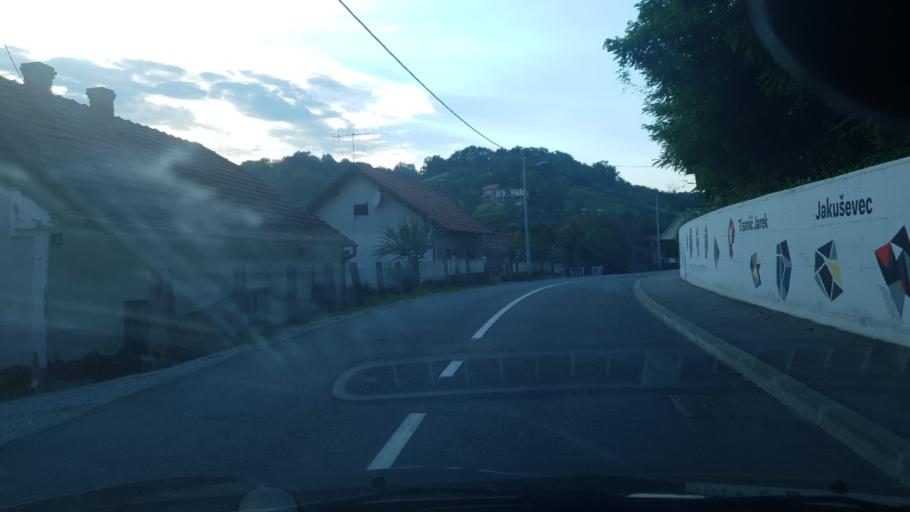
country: HR
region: Krapinsko-Zagorska
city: Zabok
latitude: 46.0202
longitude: 15.8876
